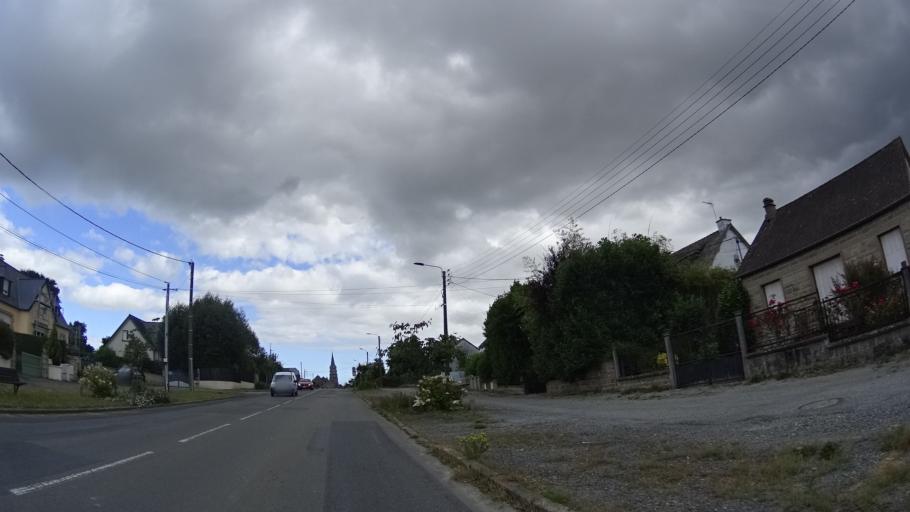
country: FR
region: Brittany
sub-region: Departement d'Ille-et-Vilaine
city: Tinteniac
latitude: 48.3243
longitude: -1.8306
